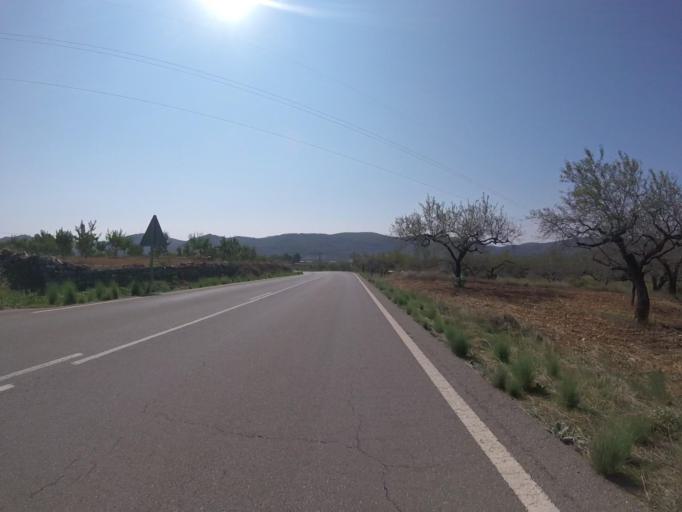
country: ES
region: Valencia
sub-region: Provincia de Castello
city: Adzaneta
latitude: 40.2281
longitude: -0.1746
